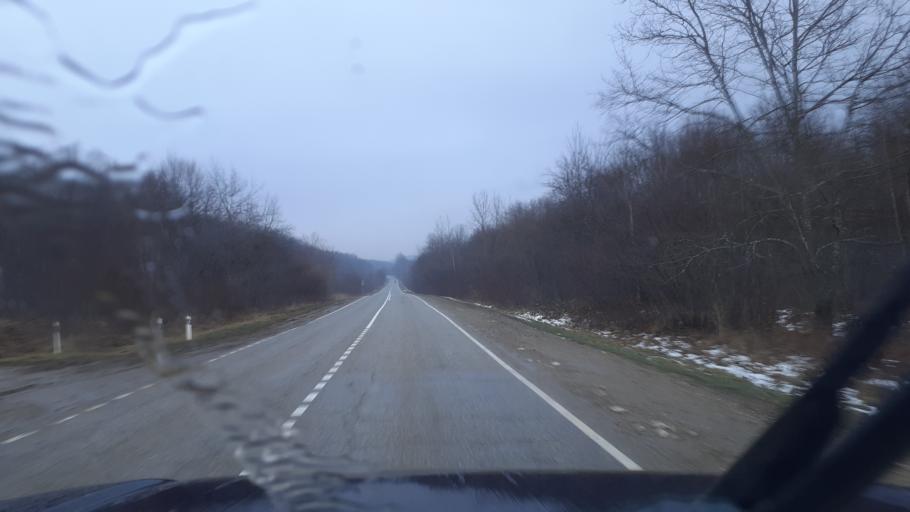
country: RU
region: Krasnodarskiy
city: Neftegorsk
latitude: 44.2767
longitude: 39.7920
